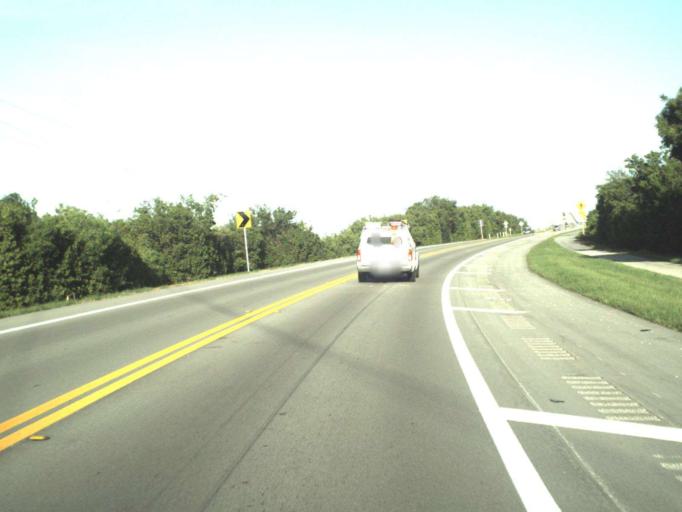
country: US
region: Florida
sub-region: Monroe County
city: Islamorada
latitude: 24.8411
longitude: -80.7872
